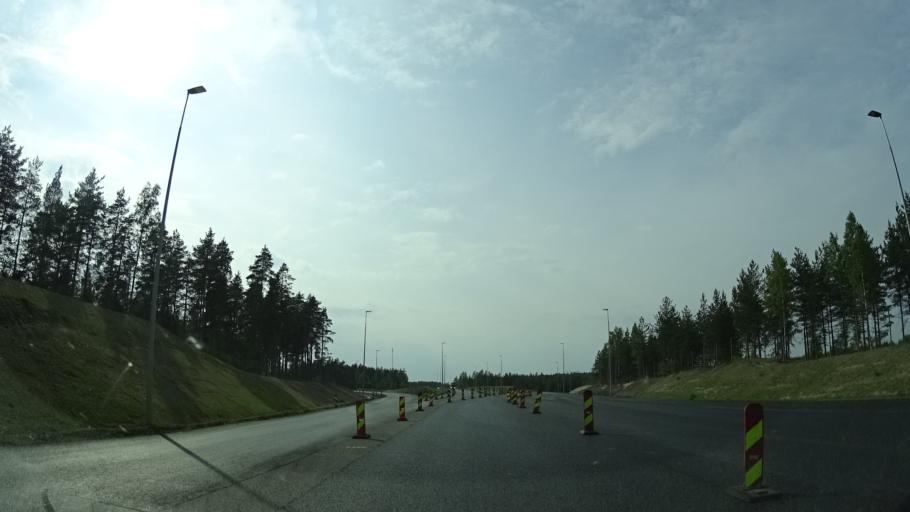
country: FI
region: South Karelia
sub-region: Lappeenranta
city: Luumaeki
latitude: 60.9288
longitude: 27.5921
